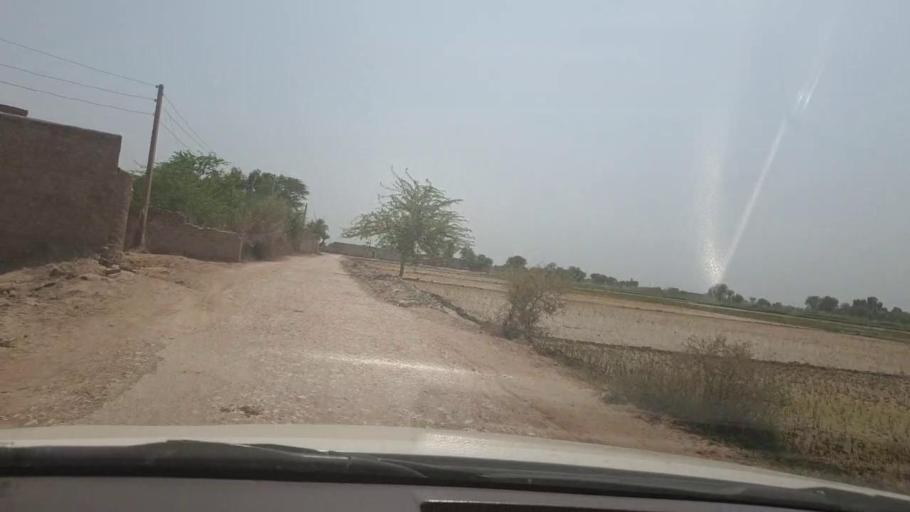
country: PK
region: Sindh
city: Shikarpur
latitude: 27.9984
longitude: 68.5892
